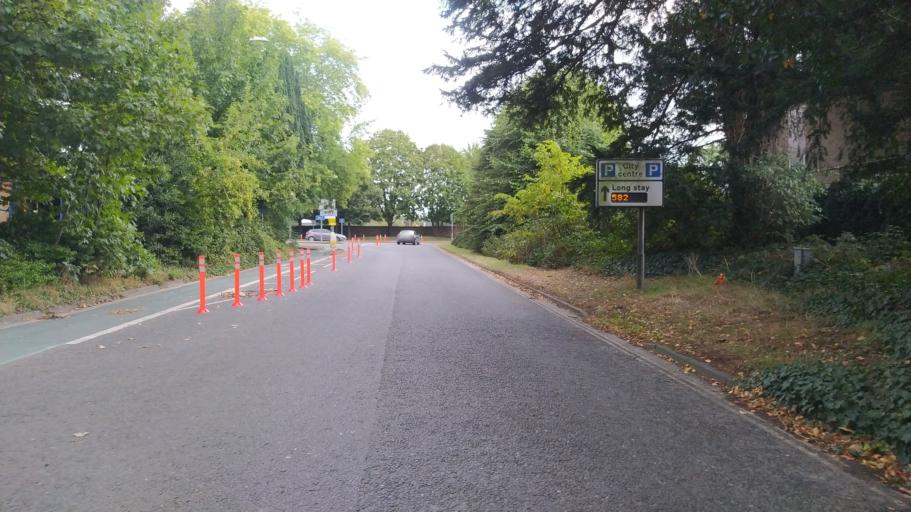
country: GB
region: England
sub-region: West Sussex
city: Chichester
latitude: 50.8411
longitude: -0.7799
